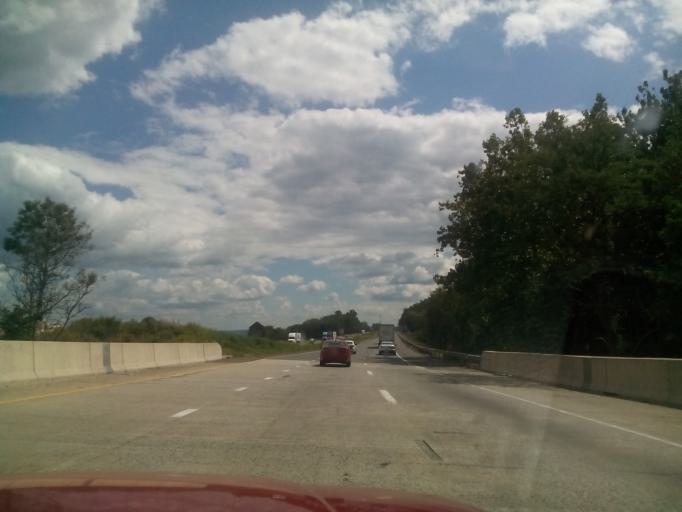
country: US
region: Pennsylvania
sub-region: Monroe County
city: Tannersville
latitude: 41.0516
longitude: -75.3166
